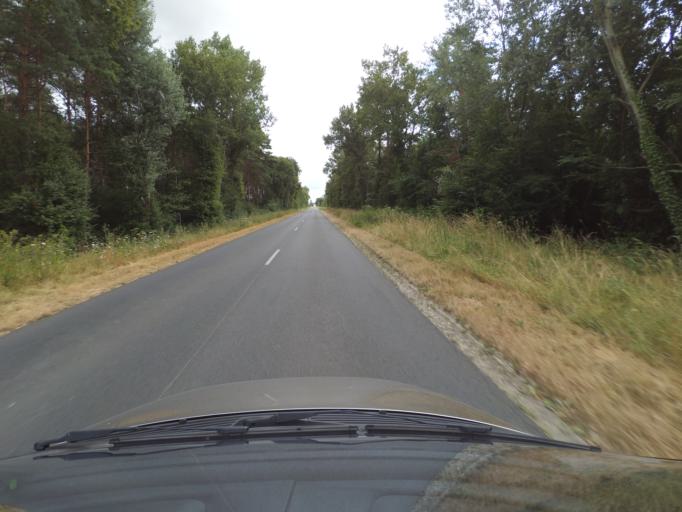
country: FR
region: Centre
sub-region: Departement d'Indre-et-Loire
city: Richelieu
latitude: 46.9784
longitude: 0.3549
